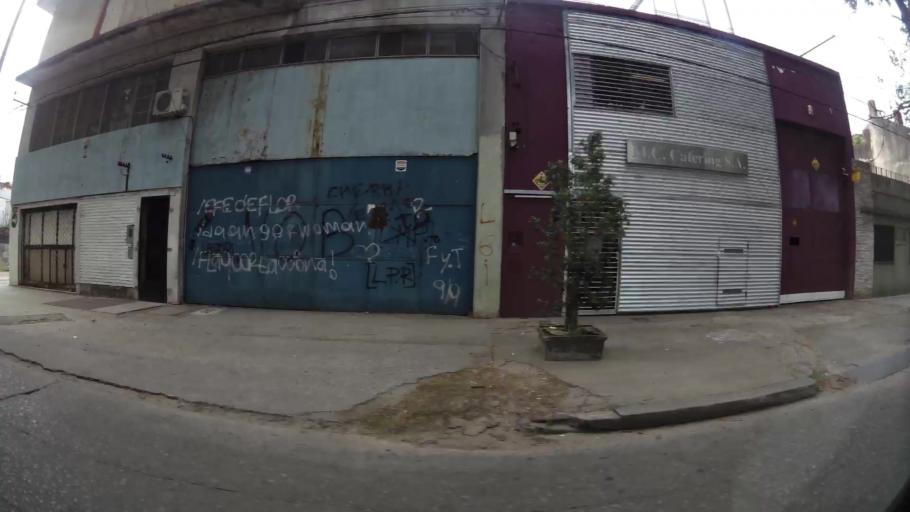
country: AR
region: Santa Fe
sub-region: Departamento de Rosario
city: Rosario
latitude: -32.9265
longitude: -60.6732
